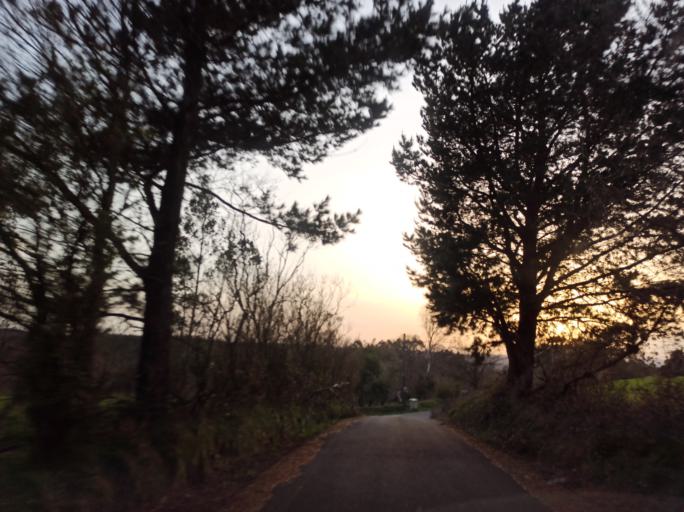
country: ES
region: Galicia
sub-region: Provincia da Coruna
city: Coiros
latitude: 43.1850
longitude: -8.1290
